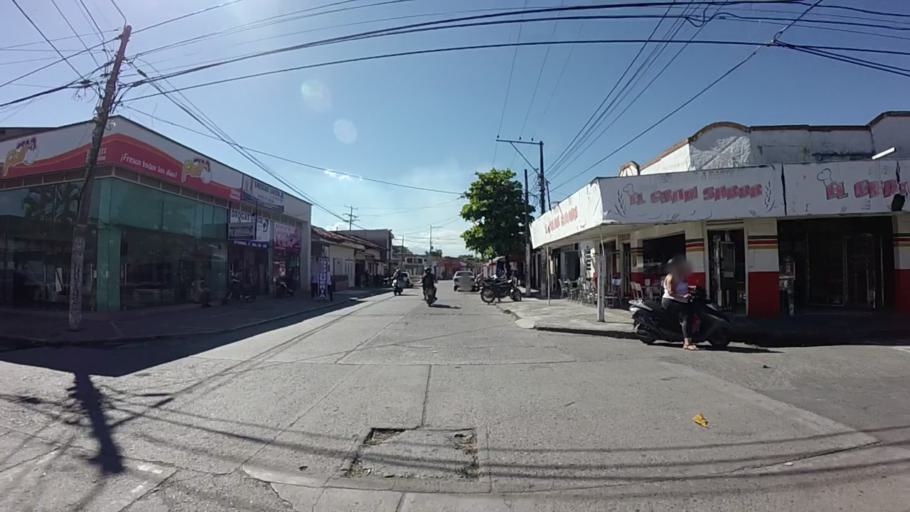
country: CO
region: Valle del Cauca
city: Cartago
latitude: 4.7407
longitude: -75.9077
